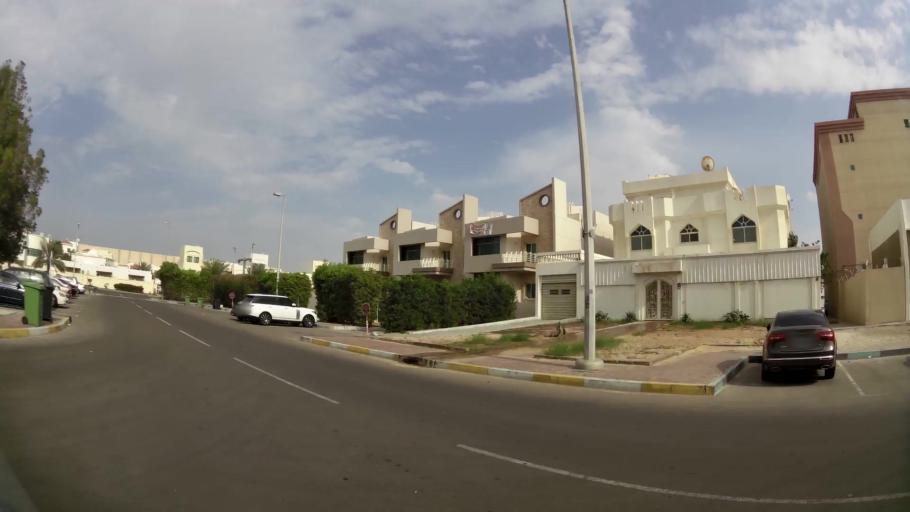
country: AE
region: Abu Dhabi
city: Abu Dhabi
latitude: 24.4677
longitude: 54.3488
